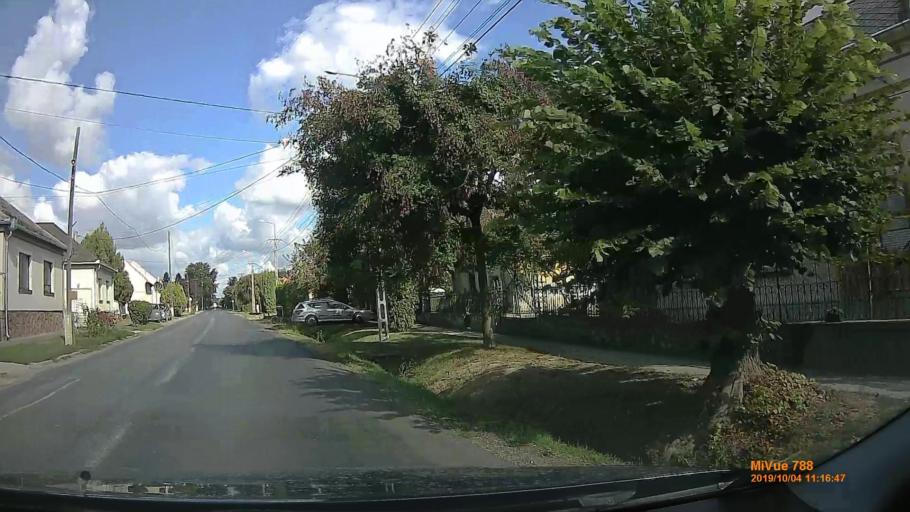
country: HU
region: Somogy
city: Kaposvar
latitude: 46.4579
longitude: 17.8056
